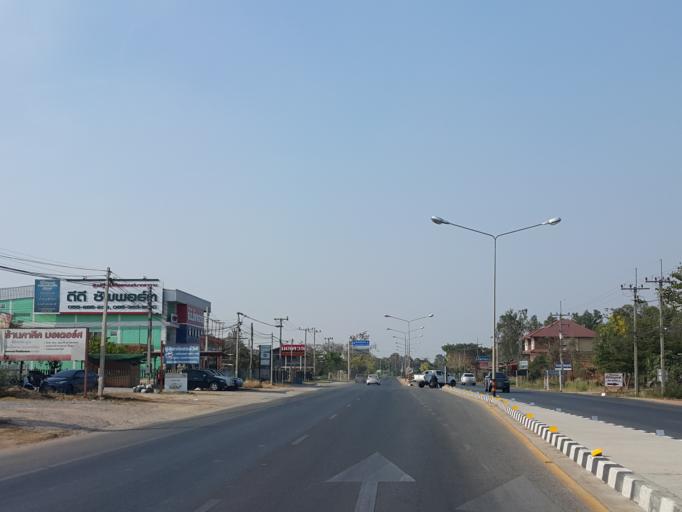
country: TH
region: Phitsanulok
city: Phitsanulok
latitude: 16.8264
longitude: 100.3320
